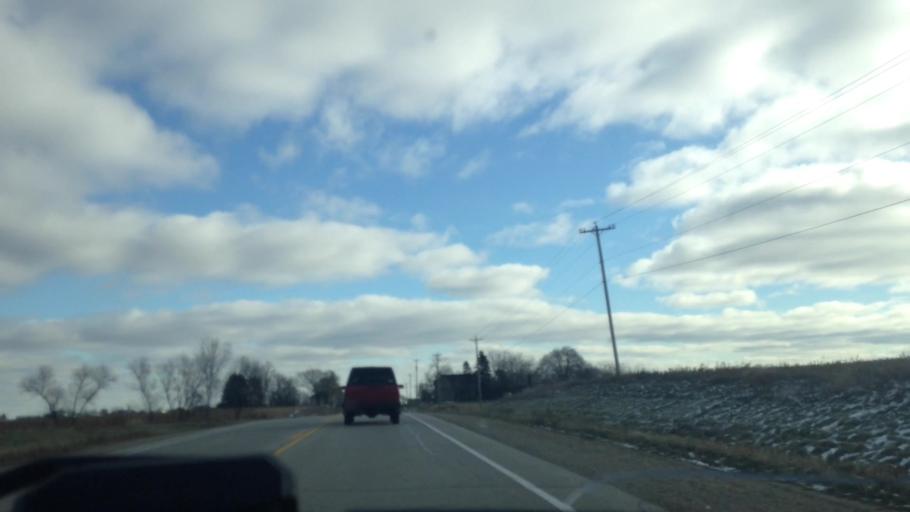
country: US
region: Wisconsin
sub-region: Washington County
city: Hartford
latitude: 43.4222
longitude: -88.3999
